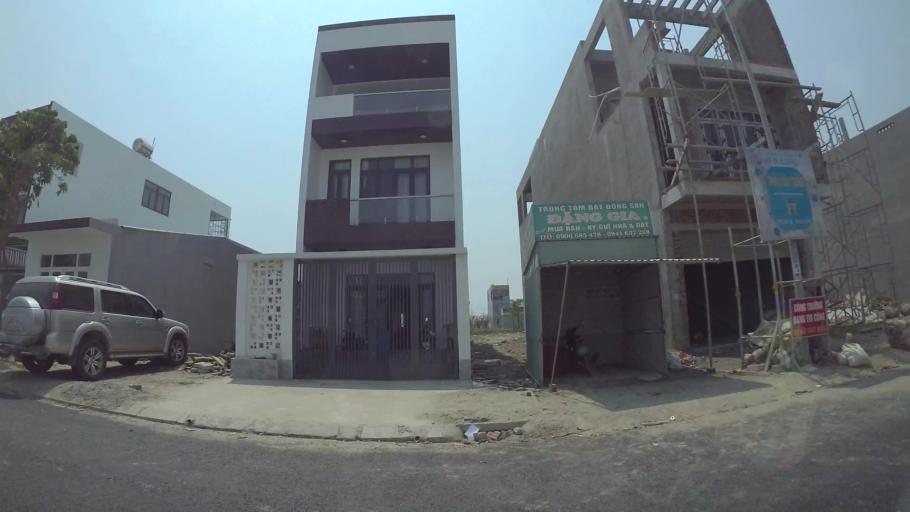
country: VN
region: Da Nang
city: Ngu Hanh Son
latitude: 16.0109
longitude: 108.2419
